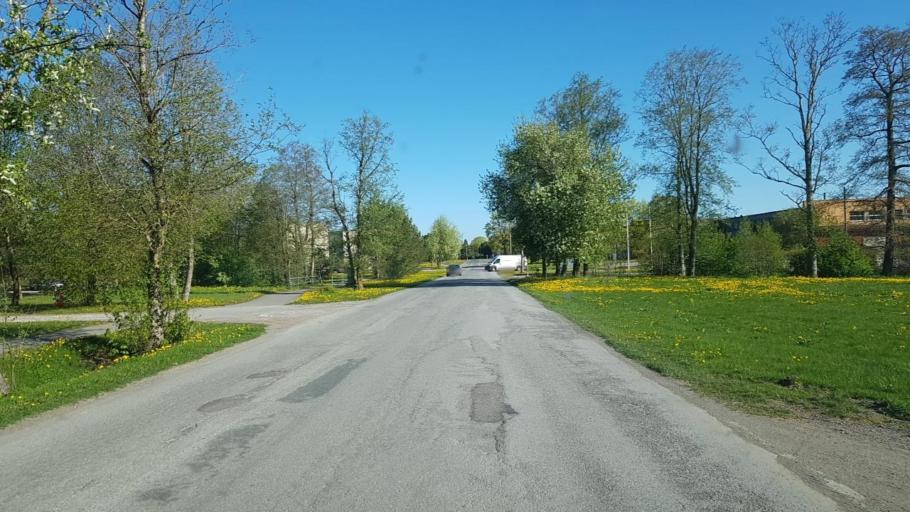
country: EE
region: Harju
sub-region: Kuusalu vald
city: Kuusalu
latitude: 59.4494
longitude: 25.3835
